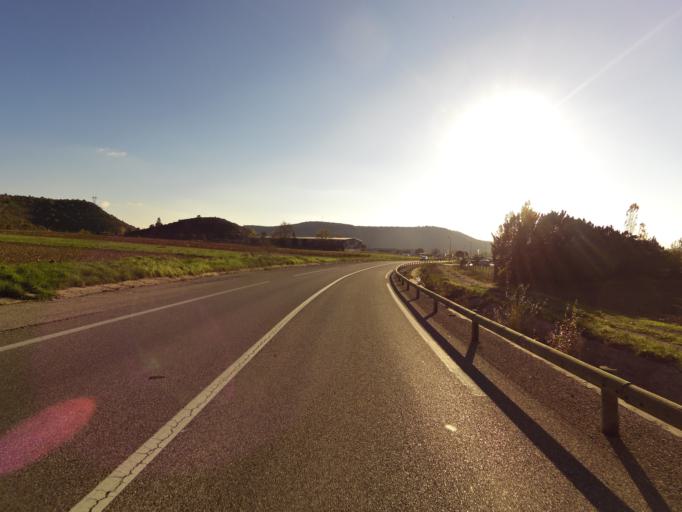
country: FR
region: Rhone-Alpes
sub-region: Departement de l'Ardeche
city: Rosieres
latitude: 44.4852
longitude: 4.2690
